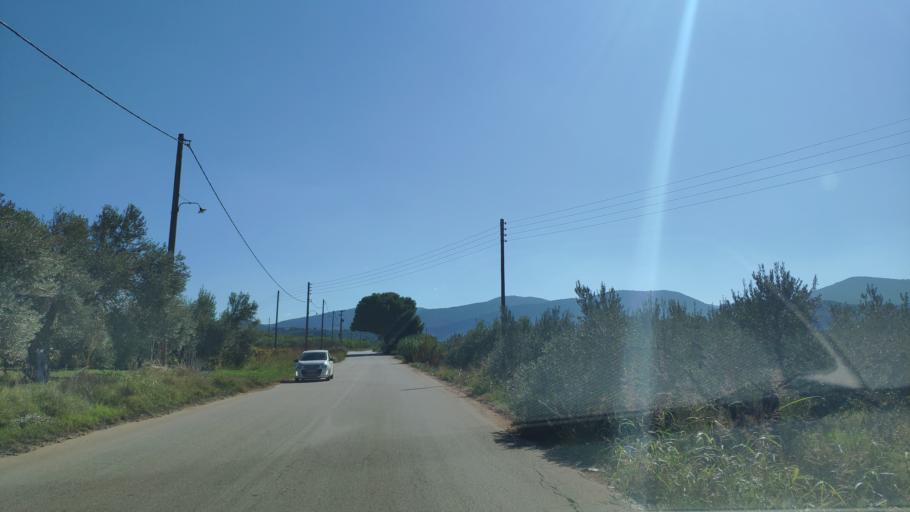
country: GR
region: Peloponnese
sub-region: Nomos Korinthias
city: Athikia
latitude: 37.8466
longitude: 22.9021
